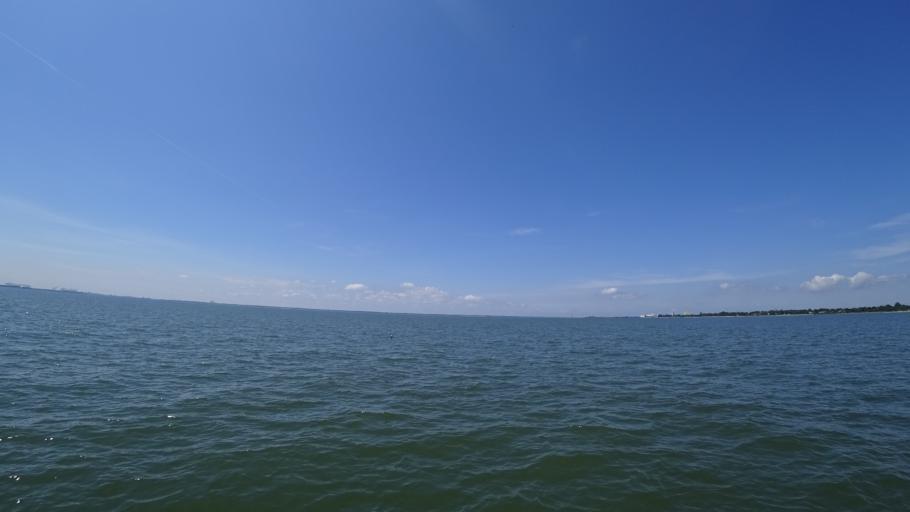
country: US
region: Virginia
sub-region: City of Newport News
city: Newport News
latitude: 36.9843
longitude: -76.3807
